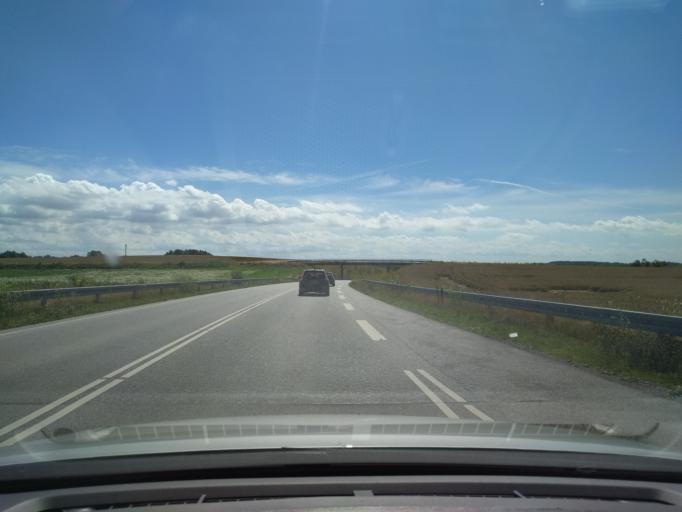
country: DK
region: Zealand
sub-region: Naestved Kommune
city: Naestved
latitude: 55.2093
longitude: 11.8147
